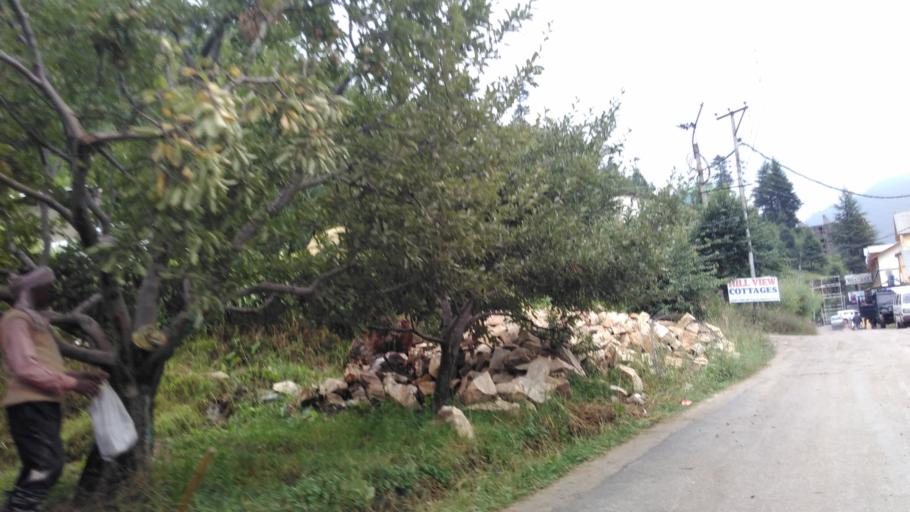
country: IN
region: Himachal Pradesh
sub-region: Kulu
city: Manali
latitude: 32.2226
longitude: 77.1845
